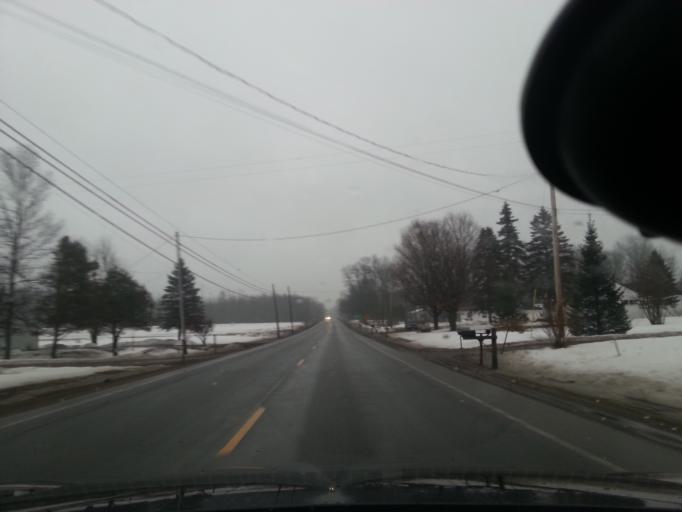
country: US
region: New York
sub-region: St. Lawrence County
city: Ogdensburg
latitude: 44.6551
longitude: -75.4475
